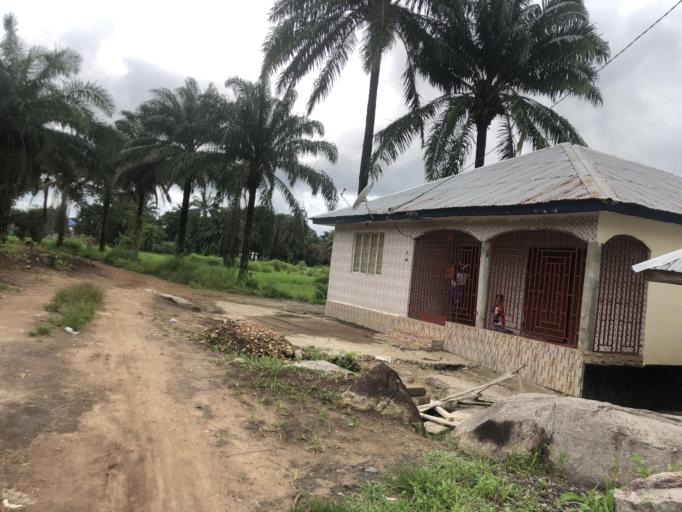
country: SL
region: Northern Province
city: Makeni
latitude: 8.9073
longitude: -12.0423
